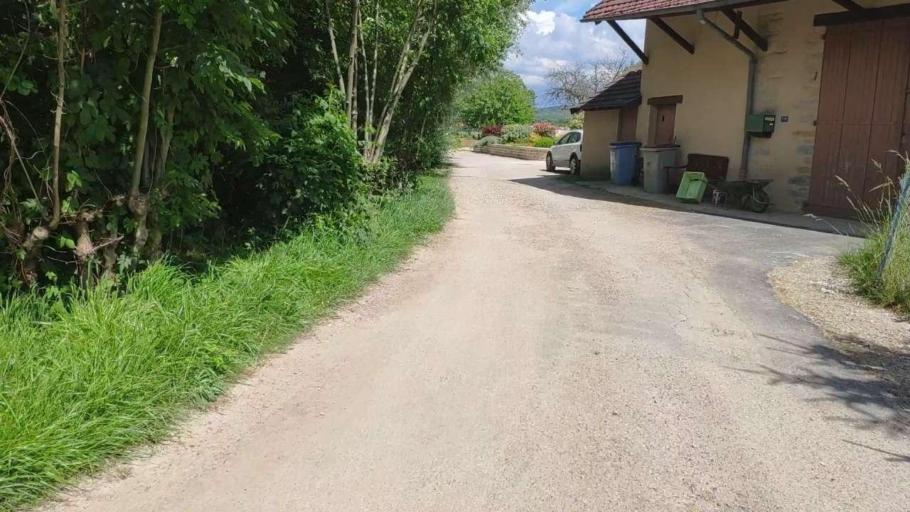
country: FR
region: Franche-Comte
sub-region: Departement du Jura
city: Bletterans
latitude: 46.7416
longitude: 5.4874
